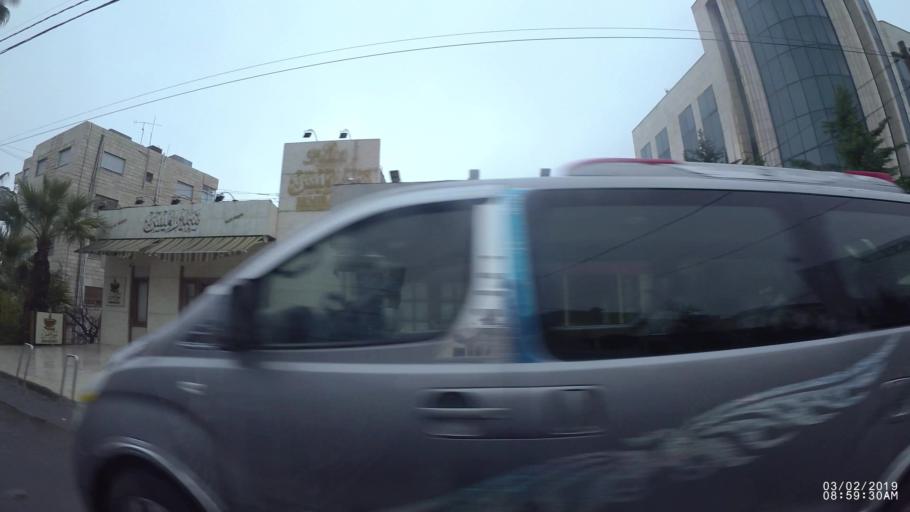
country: JO
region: Amman
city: Al Jubayhah
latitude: 31.9684
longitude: 35.8774
